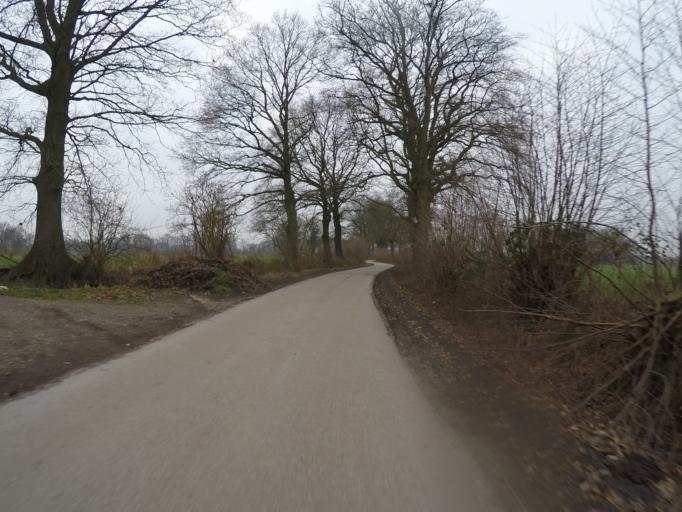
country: DE
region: Schleswig-Holstein
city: Tangstedt
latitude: 53.6836
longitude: 9.8448
